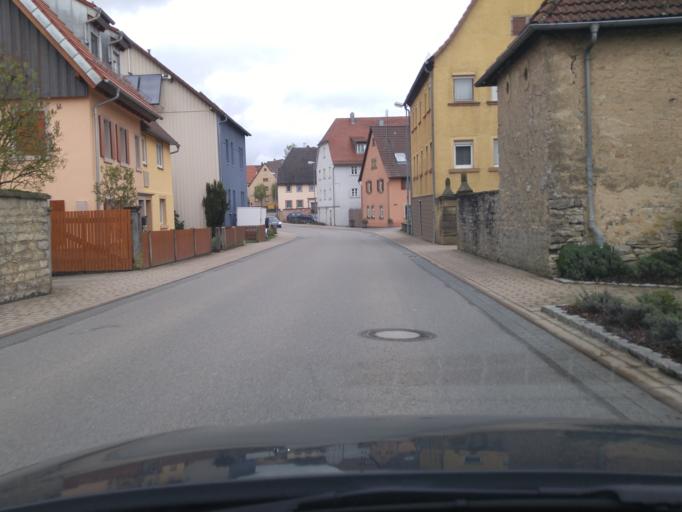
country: DE
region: Baden-Wuerttemberg
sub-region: Karlsruhe Region
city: Huffenhardt
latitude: 49.2896
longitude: 9.0838
